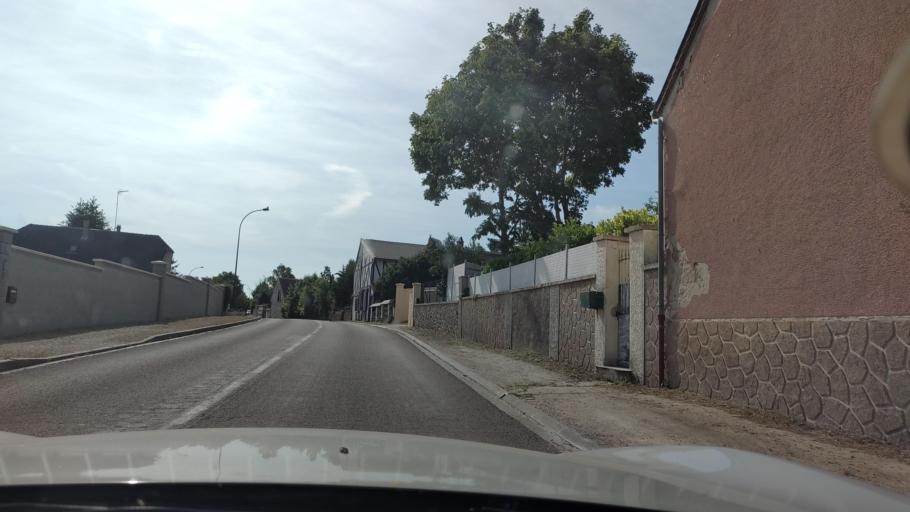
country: FR
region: Champagne-Ardenne
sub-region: Departement de l'Aube
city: Nogent-sur-Seine
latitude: 48.4480
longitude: 3.6151
